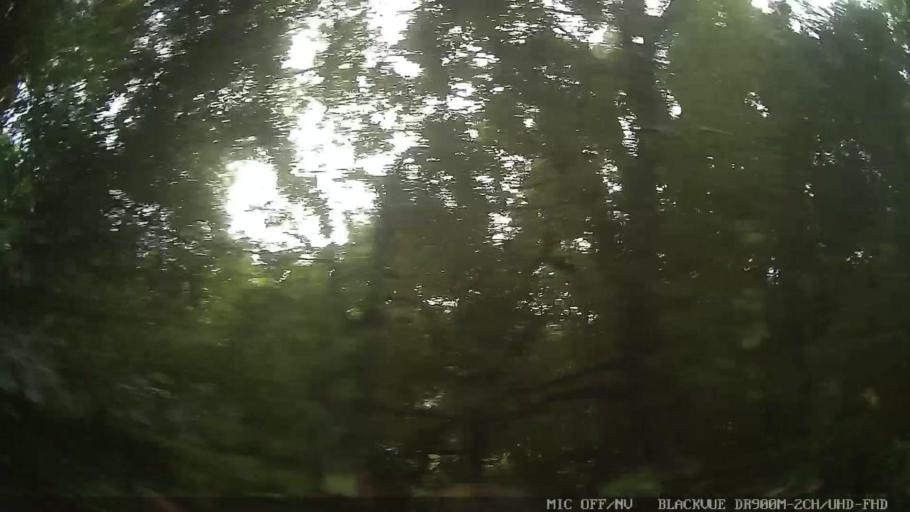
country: BR
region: Sao Paulo
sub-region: Rio Grande Da Serra
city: Rio Grande da Serra
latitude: -23.6906
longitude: -46.3192
